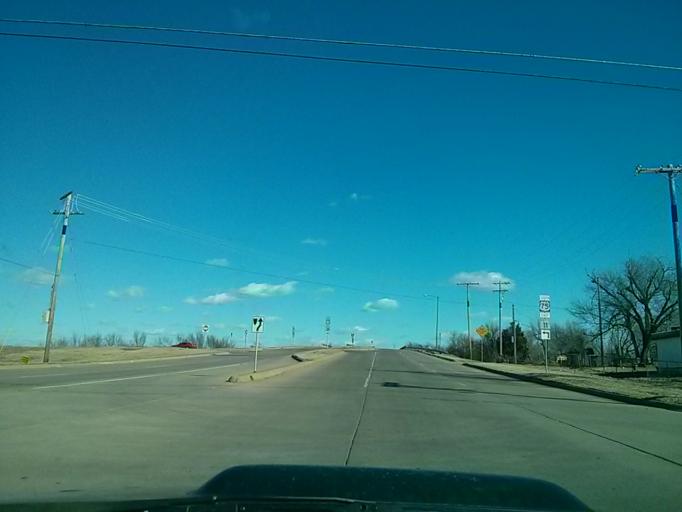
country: US
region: Oklahoma
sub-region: Tulsa County
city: Turley
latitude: 36.2061
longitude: -95.9494
